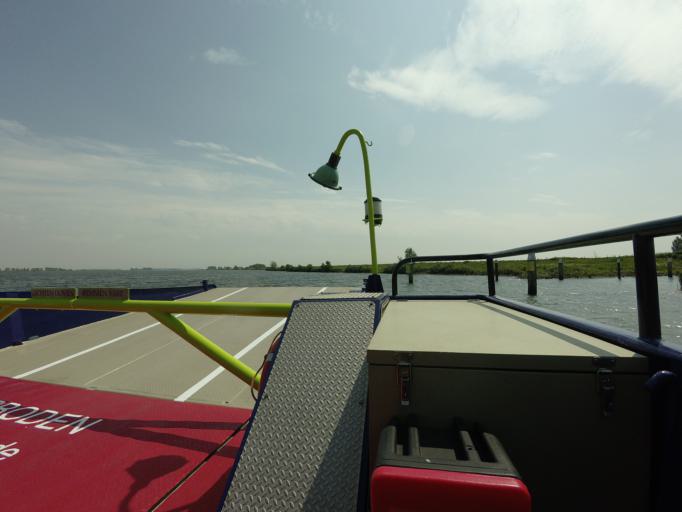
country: NL
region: South Holland
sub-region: Gemeente Spijkenisse
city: Spijkenisse
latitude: 51.7444
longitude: 4.3231
